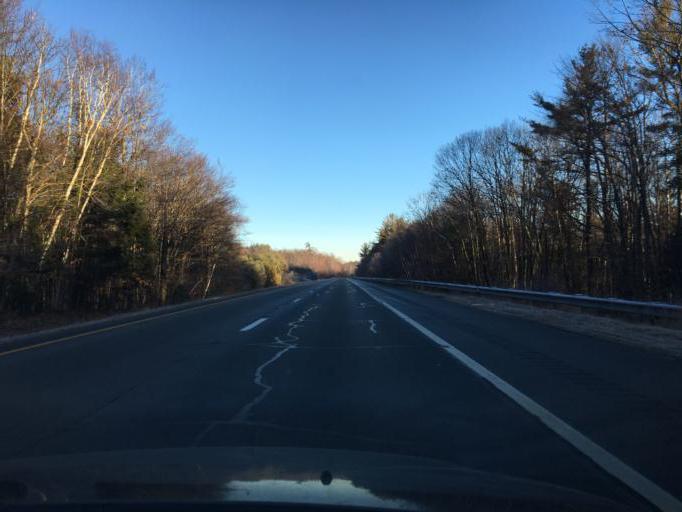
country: US
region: New Hampshire
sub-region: Belknap County
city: Sanbornton
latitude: 43.5454
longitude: -71.6157
